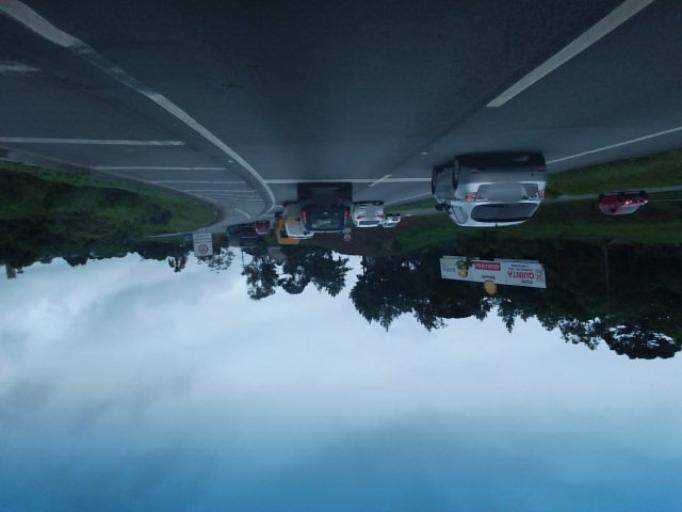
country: BR
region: Parana
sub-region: Sao Jose Dos Pinhais
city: Sao Jose dos Pinhais
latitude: -25.8461
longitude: -49.0626
